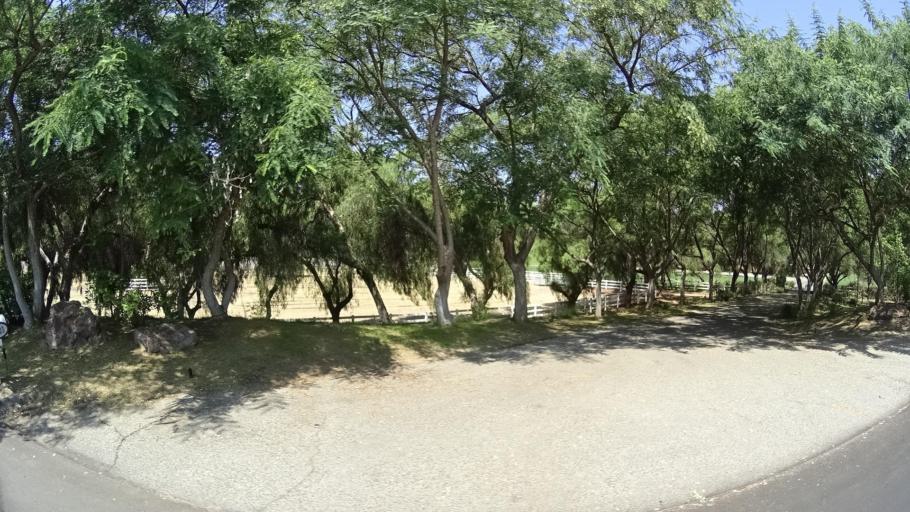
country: US
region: California
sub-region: San Diego County
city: Bonsall
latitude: 33.2787
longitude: -117.1870
